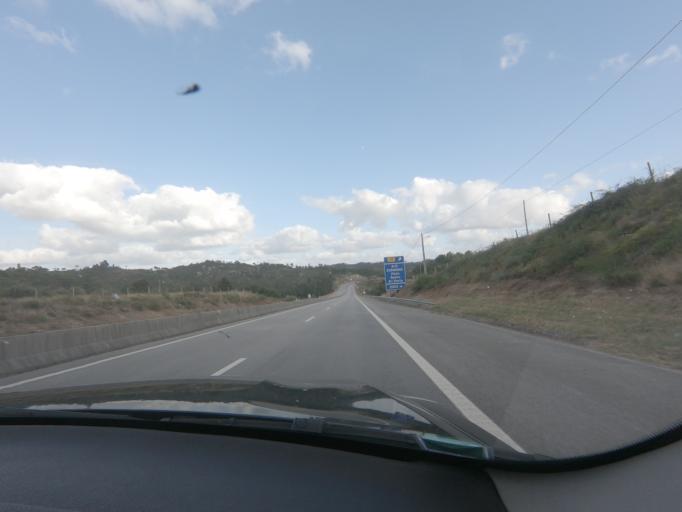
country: PT
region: Viseu
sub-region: Viseu
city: Viseu
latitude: 40.6439
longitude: -7.9637
